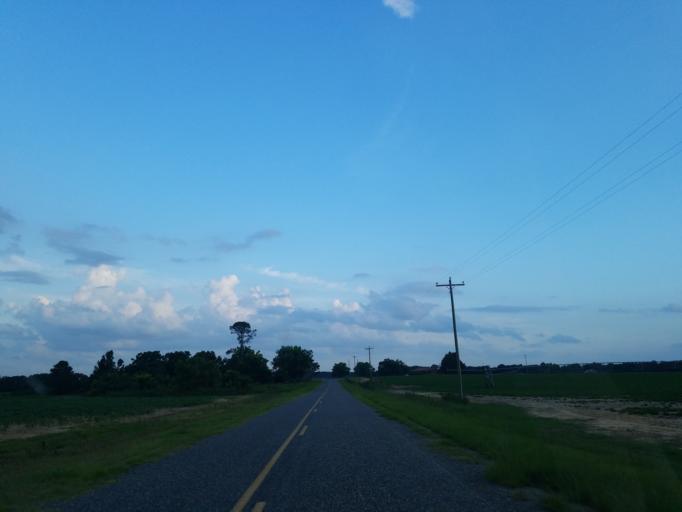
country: US
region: Georgia
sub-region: Dooly County
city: Unadilla
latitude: 32.1648
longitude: -83.7210
